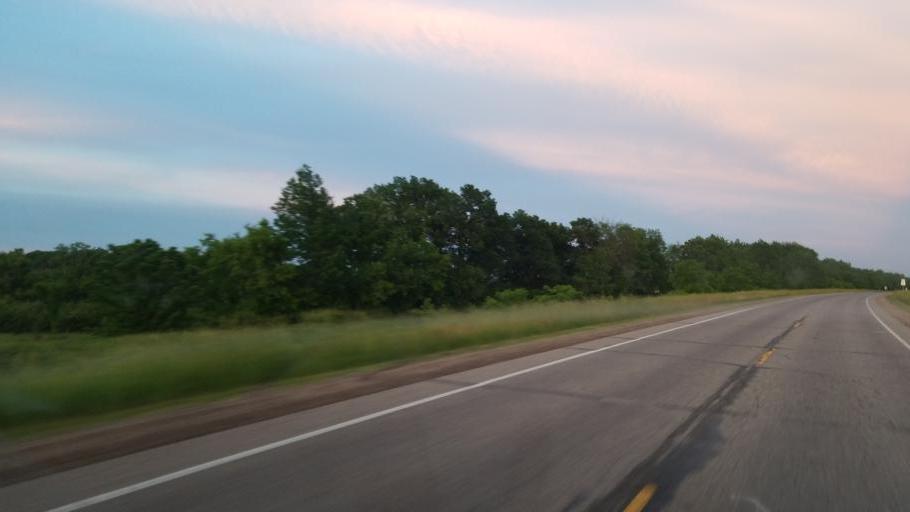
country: US
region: Wisconsin
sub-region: Juneau County
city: Elroy
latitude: 43.7561
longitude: -90.2950
